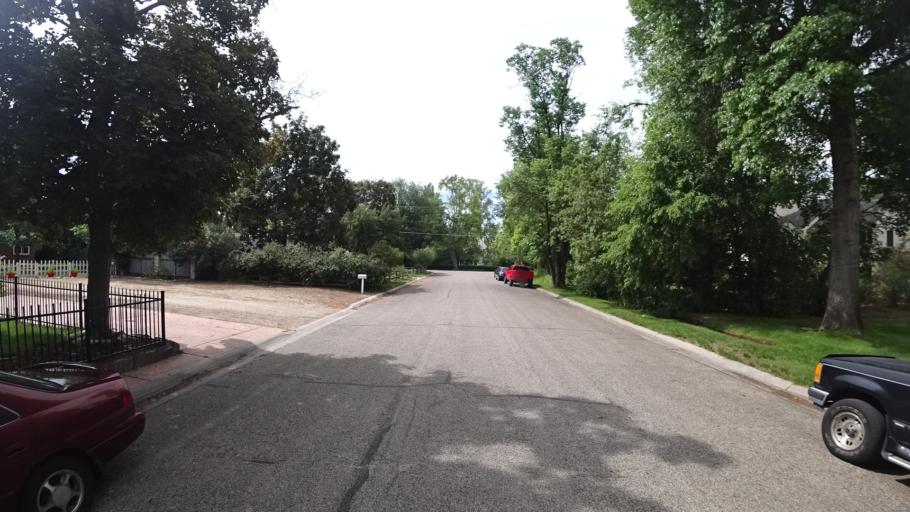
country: US
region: Idaho
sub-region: Ada County
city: Boise
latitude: 43.5904
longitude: -116.2000
